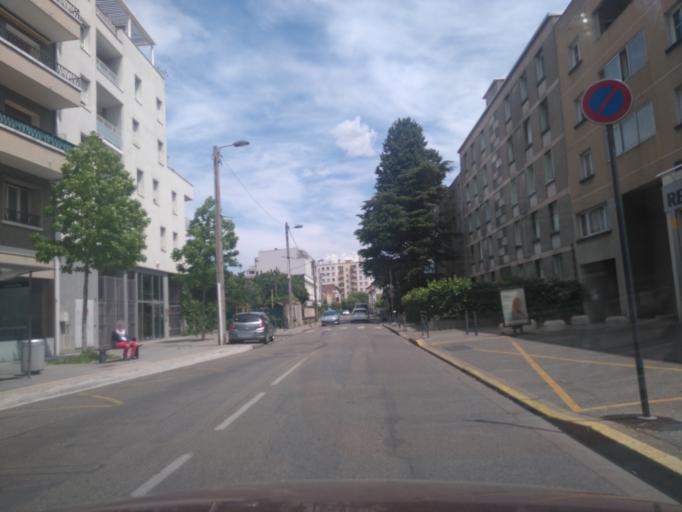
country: FR
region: Rhone-Alpes
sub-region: Departement de l'Isere
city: La Tronche
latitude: 45.1817
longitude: 5.7450
